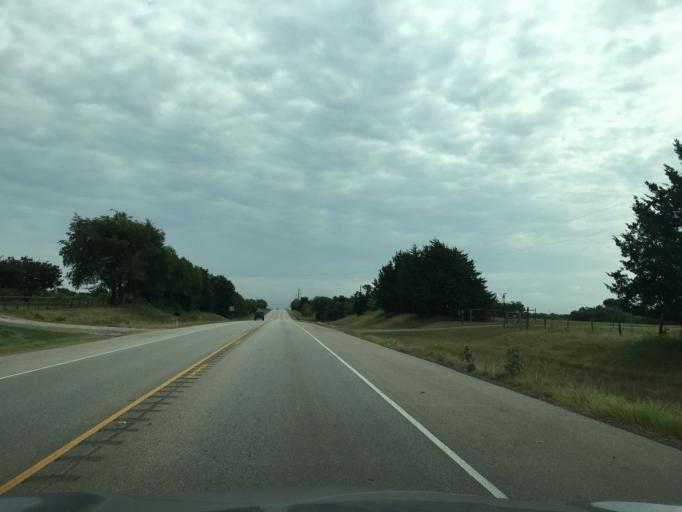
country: US
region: Texas
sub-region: Collin County
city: Anna
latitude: 33.3234
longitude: -96.4958
